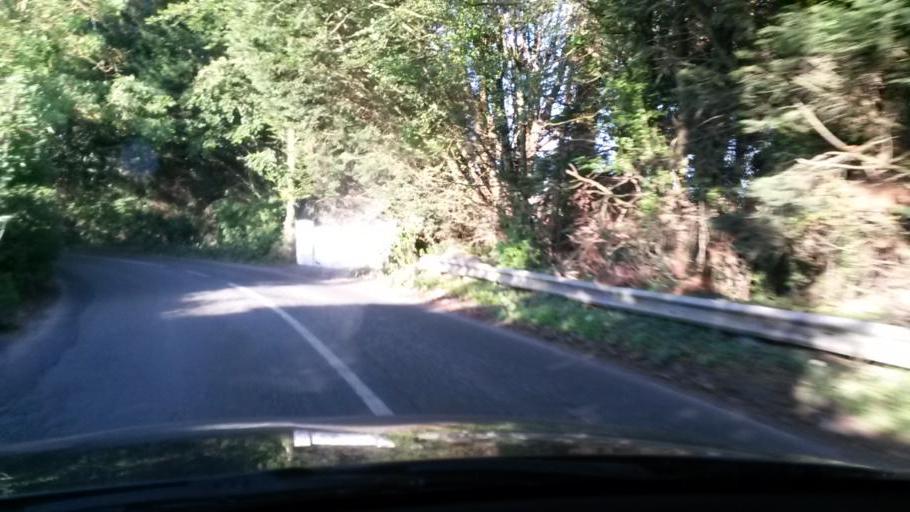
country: IE
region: Leinster
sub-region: Fingal County
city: Blanchardstown
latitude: 53.4306
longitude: -6.3626
